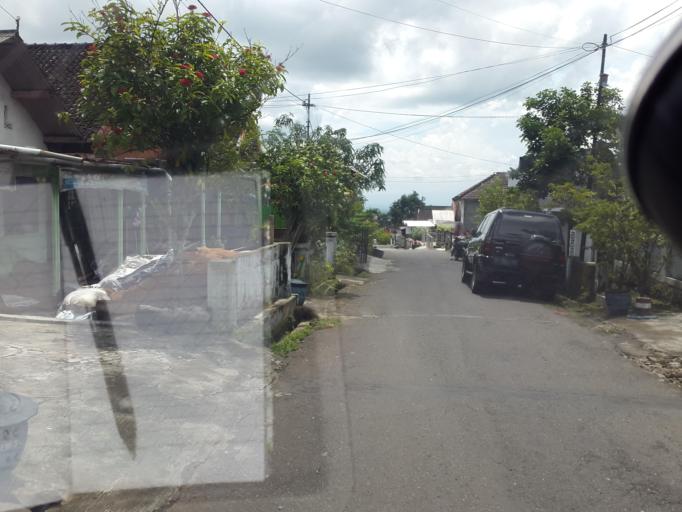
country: ID
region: East Java
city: Madiun
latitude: -7.6491
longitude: 111.3208
